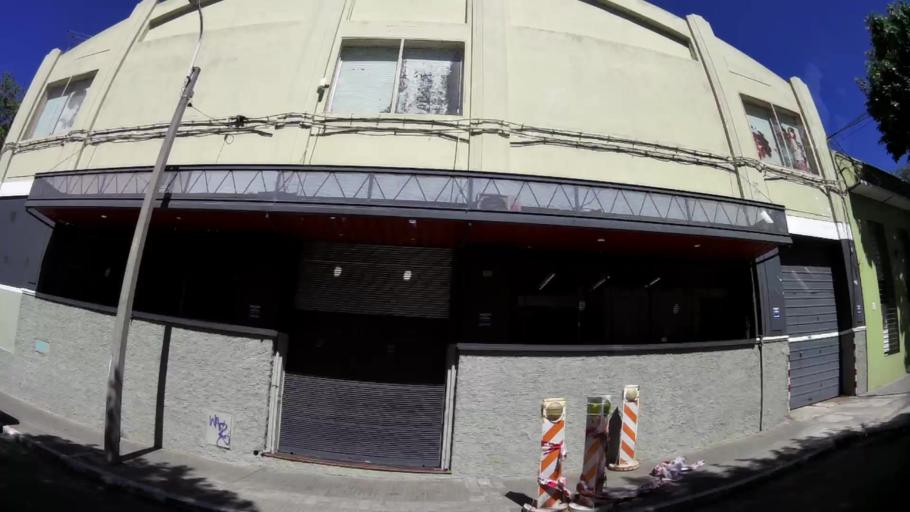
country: UY
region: Montevideo
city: Montevideo
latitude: -34.9083
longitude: -56.1773
